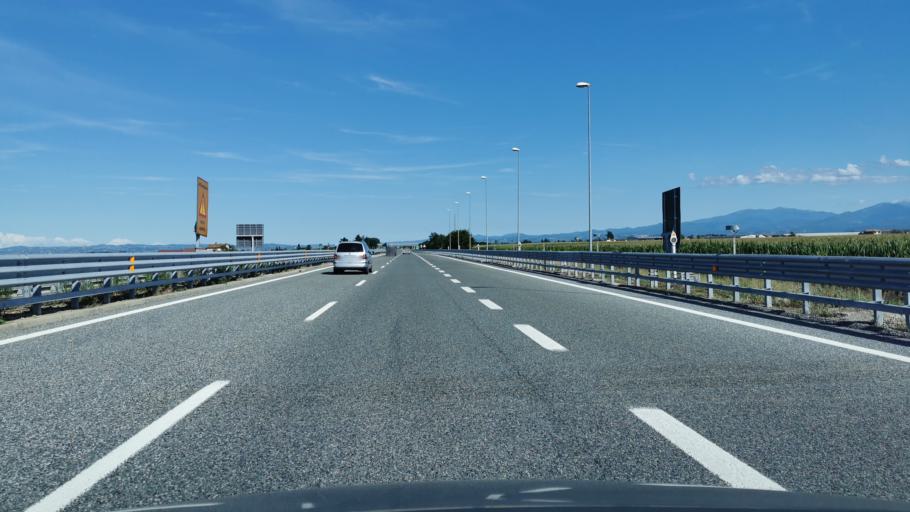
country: IT
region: Piedmont
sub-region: Provincia di Cuneo
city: Montanera
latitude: 44.4752
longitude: 7.6962
